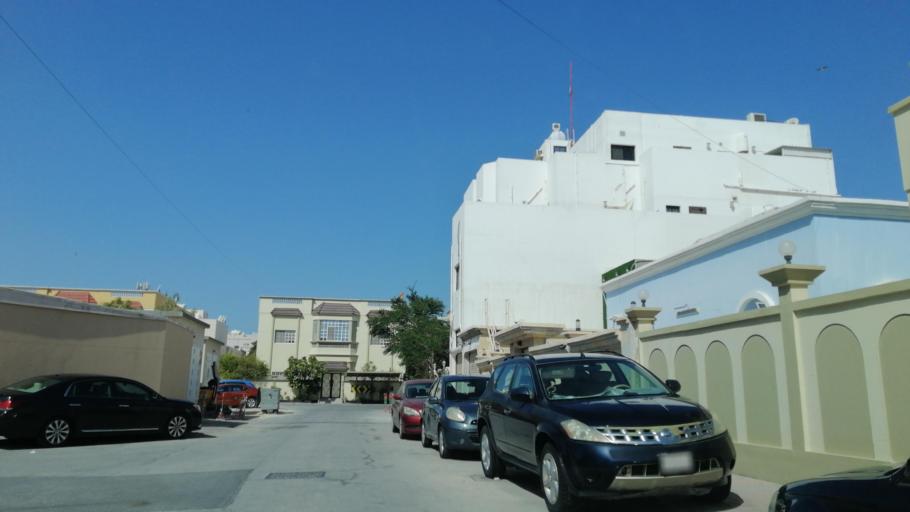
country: BH
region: Muharraq
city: Al Hadd
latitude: 26.2490
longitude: 50.6389
